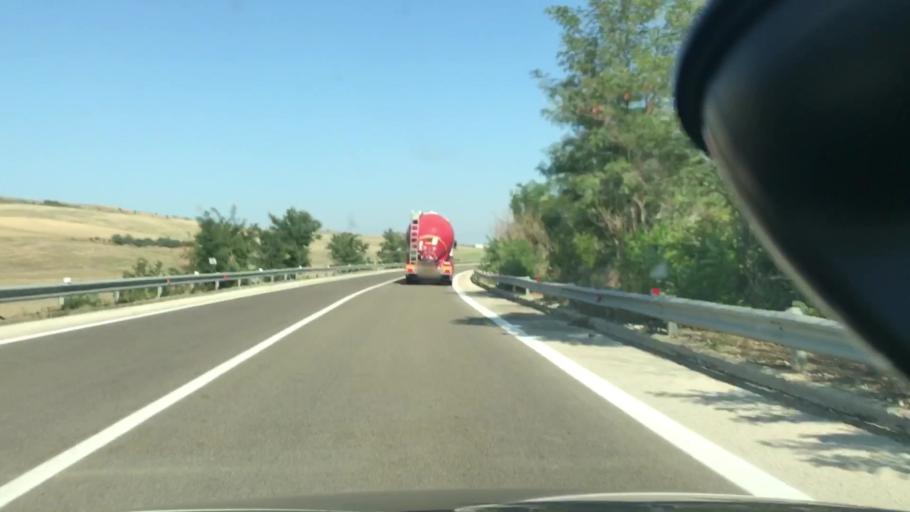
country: IT
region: Basilicate
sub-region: Provincia di Matera
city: Irsina
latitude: 40.7940
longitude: 16.2781
